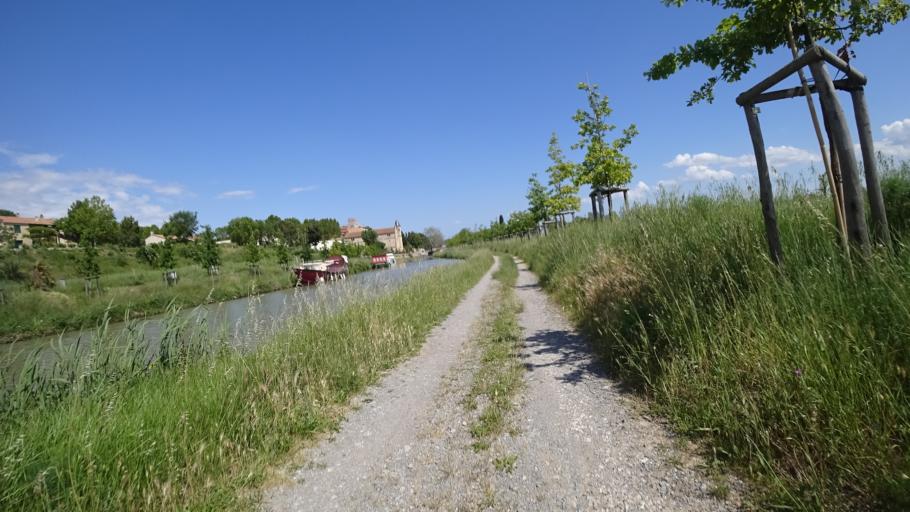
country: FR
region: Languedoc-Roussillon
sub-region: Departement de l'Aude
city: Canet
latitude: 43.2476
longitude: 2.8558
